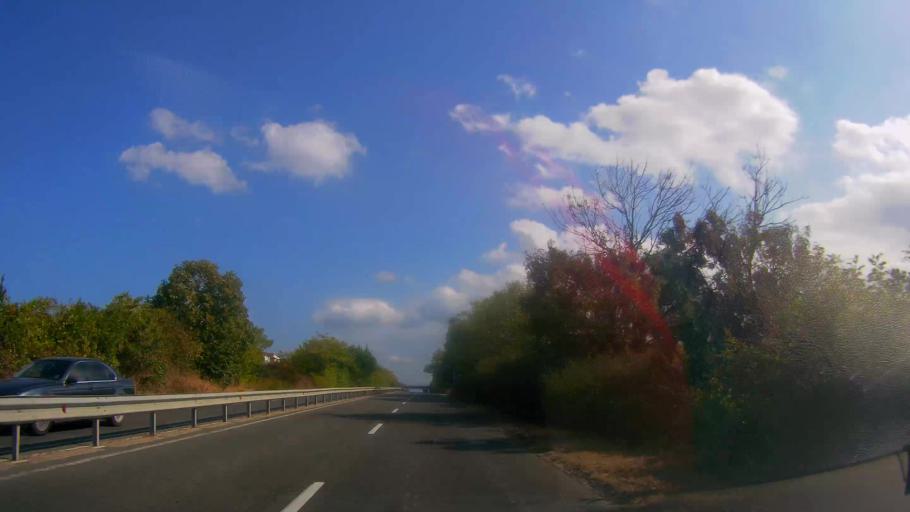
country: BG
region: Burgas
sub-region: Obshtina Sozopol
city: Chernomorets
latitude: 42.4422
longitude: 27.6327
